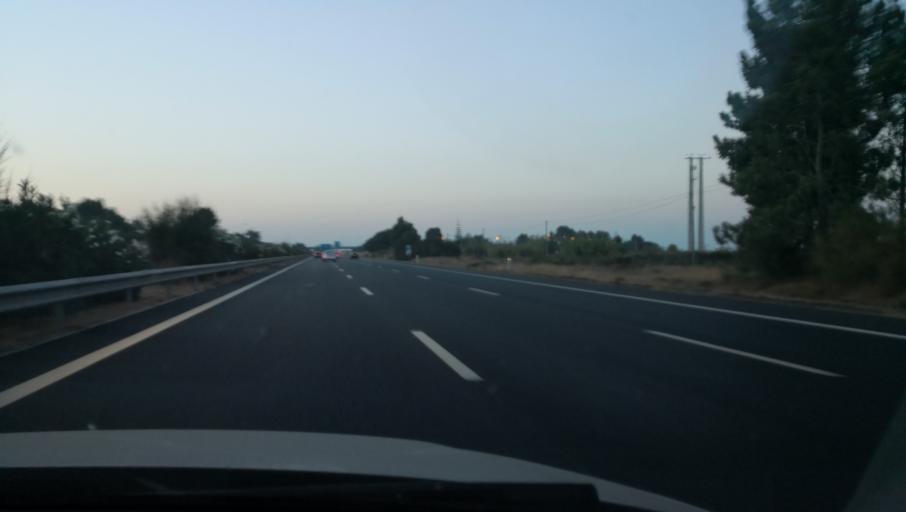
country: PT
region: Setubal
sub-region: Palmela
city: Pinhal Novo
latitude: 38.6514
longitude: -8.8889
